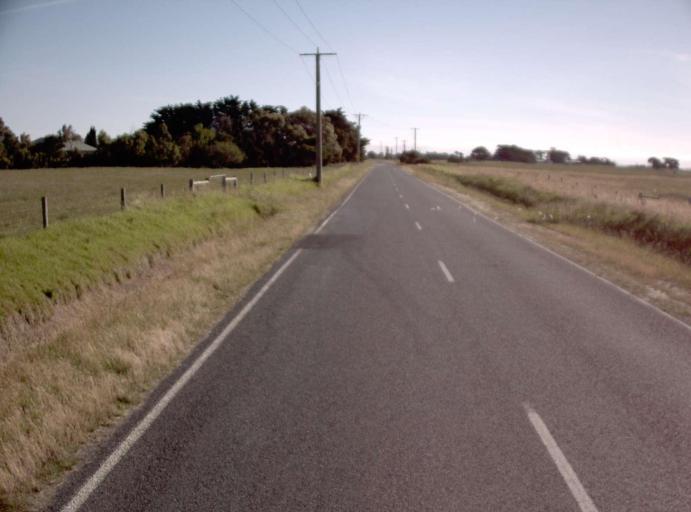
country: AU
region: Victoria
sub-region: Latrobe
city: Morwell
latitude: -38.6752
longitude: 146.3943
